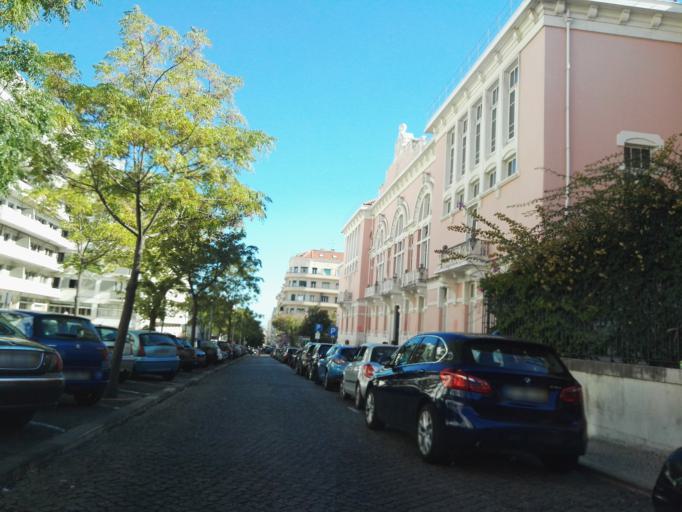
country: PT
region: Lisbon
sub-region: Lisbon
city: Lisbon
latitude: 38.7270
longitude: -9.1568
